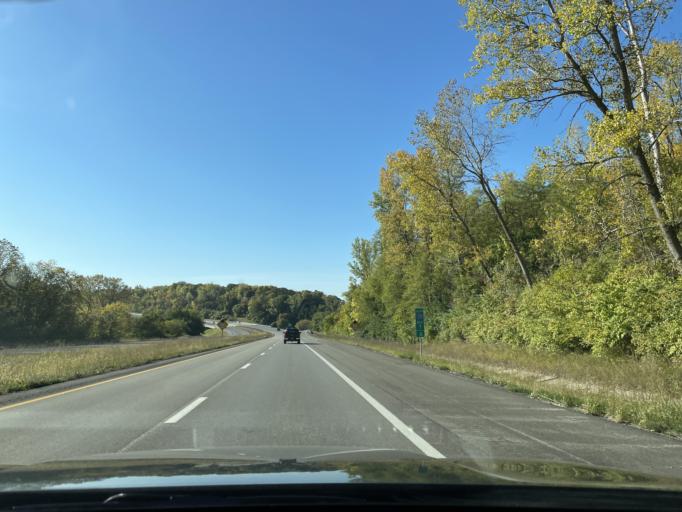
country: US
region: Missouri
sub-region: Buchanan County
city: Saint Joseph
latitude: 39.7857
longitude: -94.8693
